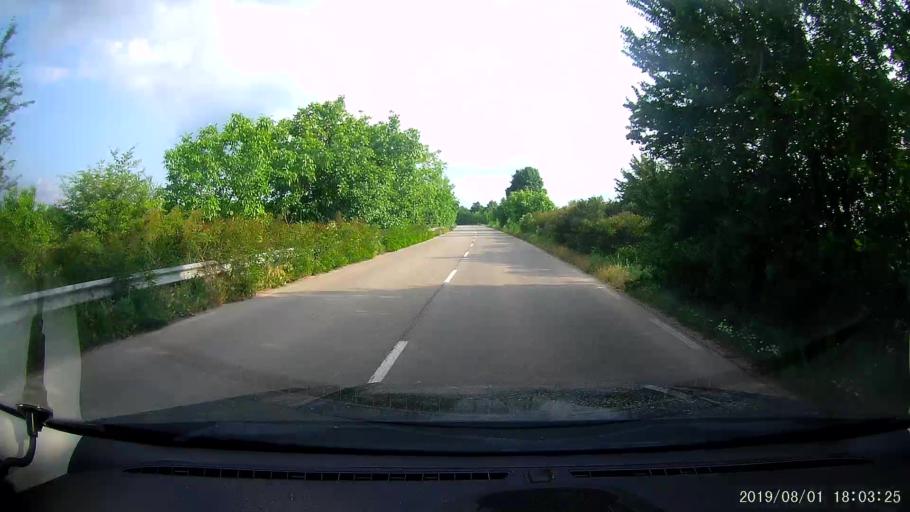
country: BG
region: Silistra
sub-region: Obshtina Alfatar
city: Alfatar
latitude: 43.9279
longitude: 27.2891
